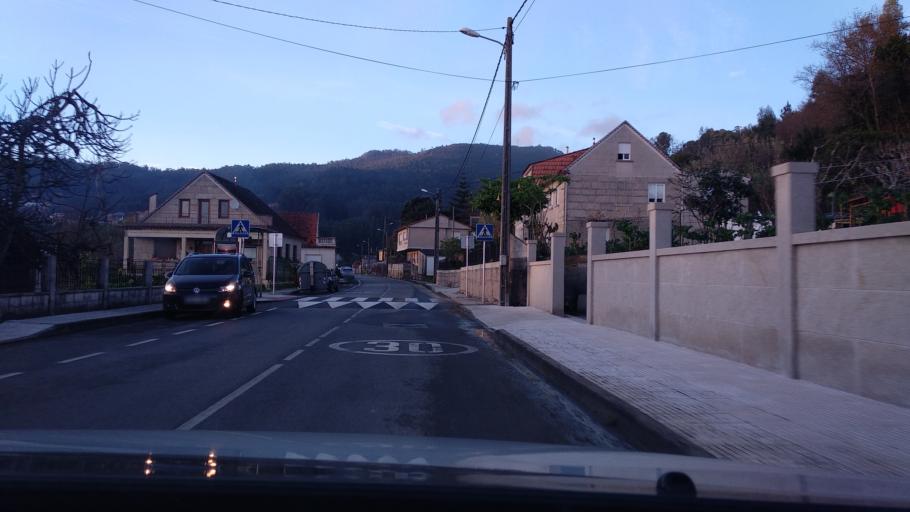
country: ES
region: Galicia
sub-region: Provincia de Pontevedra
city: Moana
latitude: 42.2975
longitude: -8.7239
